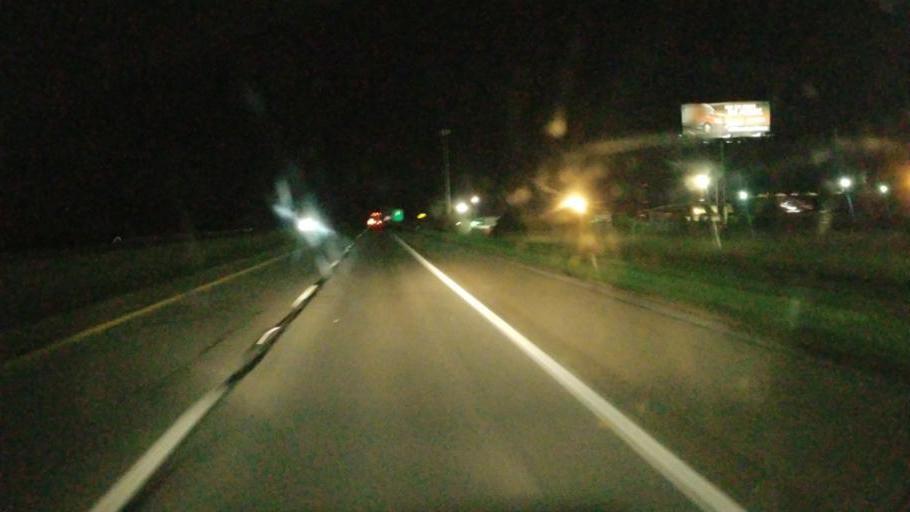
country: US
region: Ohio
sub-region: Clark County
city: Springfield
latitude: 39.8937
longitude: -83.8256
